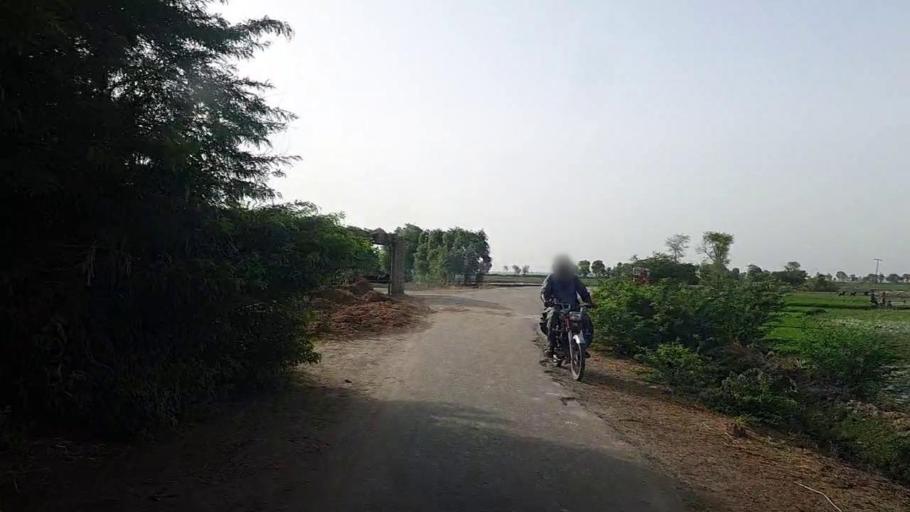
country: PK
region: Sindh
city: Khairpur Nathan Shah
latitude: 27.1082
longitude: 67.7918
